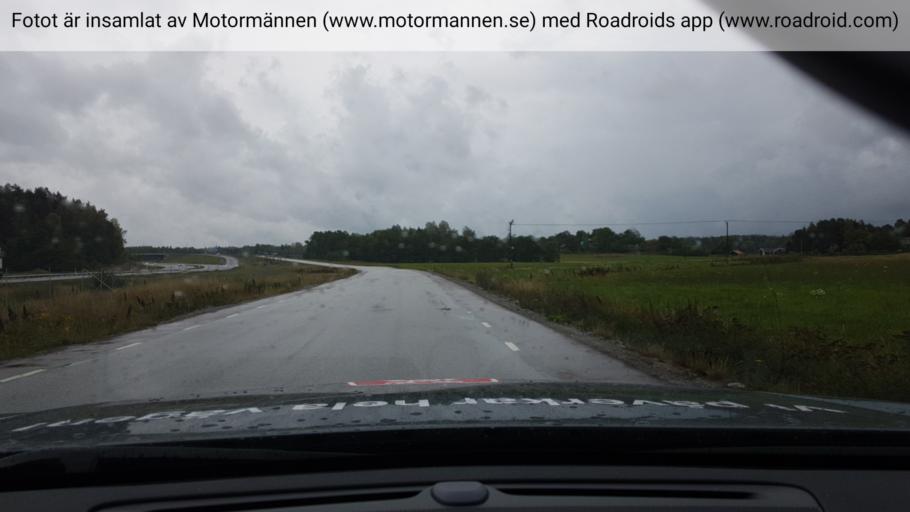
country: SE
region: Stockholm
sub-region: Haninge Kommun
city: Jordbro
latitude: 59.0641
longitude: 18.0544
